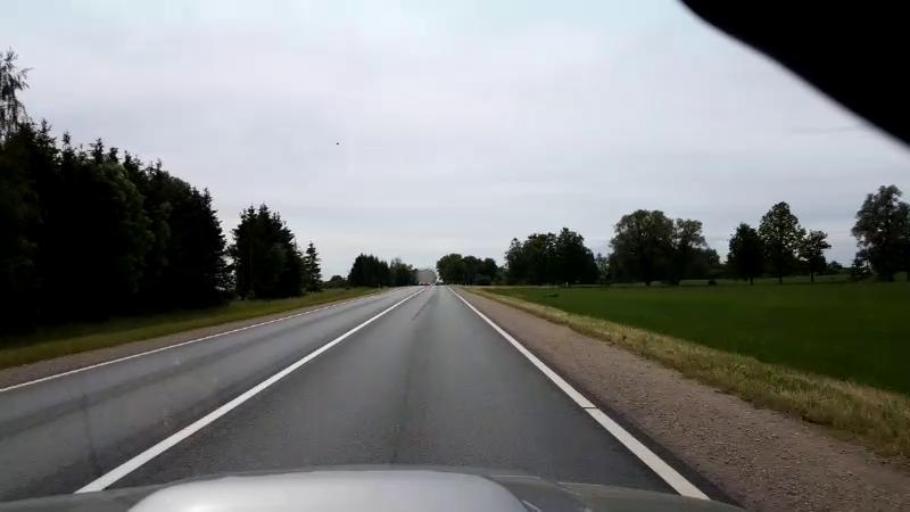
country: LV
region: Lecava
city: Iecava
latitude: 56.5544
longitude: 24.1733
